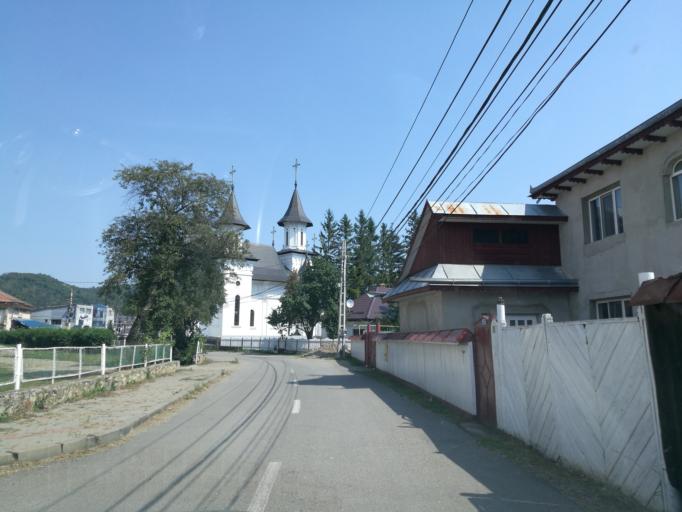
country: RO
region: Neamt
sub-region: Oras Targu Neamt
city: Humulesti
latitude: 47.1978
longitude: 26.3520
